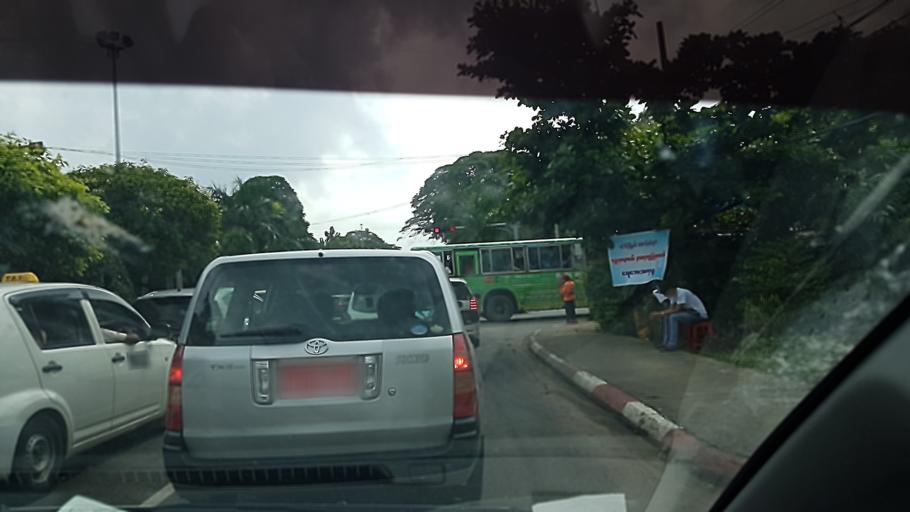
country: MM
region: Yangon
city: Yangon
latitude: 16.7928
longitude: 96.1401
